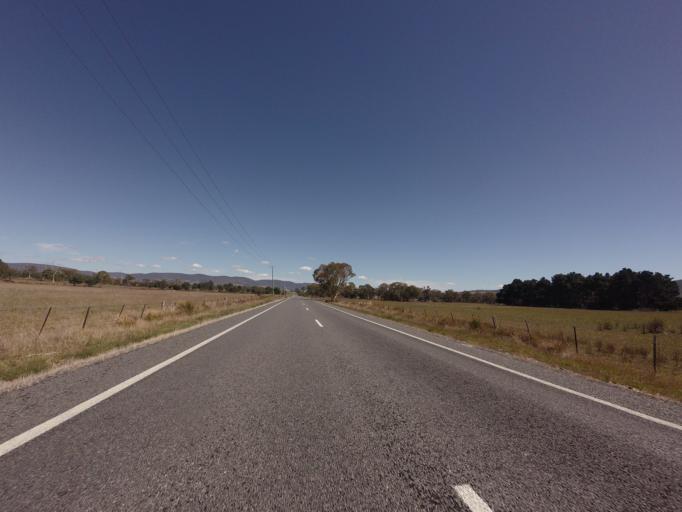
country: AU
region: Tasmania
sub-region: Northern Midlands
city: Evandale
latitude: -41.7652
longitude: 147.7456
